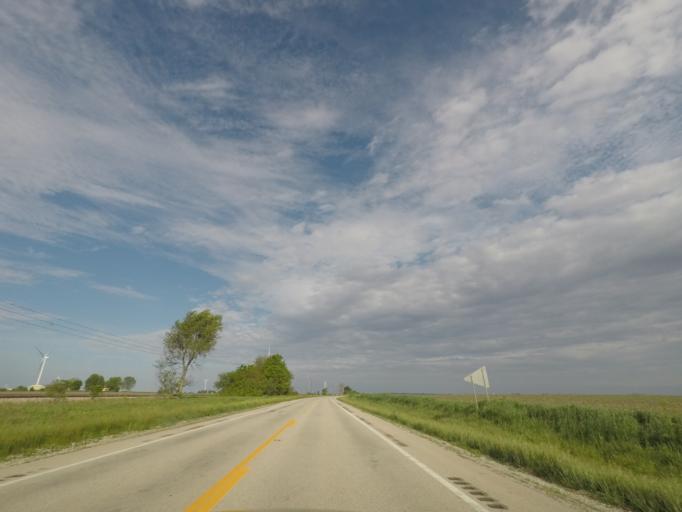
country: US
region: Illinois
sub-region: Logan County
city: Mount Pulaski
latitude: 39.9852
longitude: -89.2223
